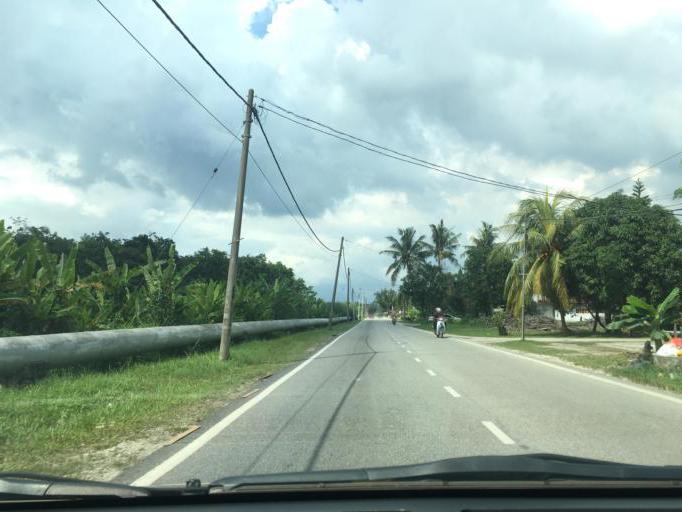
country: MY
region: Selangor
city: Kampung Baru Subang
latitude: 3.1411
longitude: 101.4461
